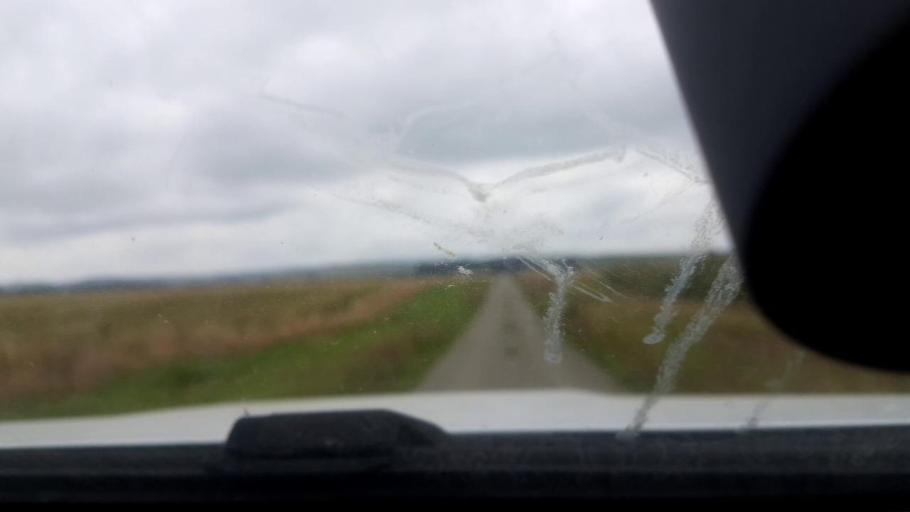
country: NZ
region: Canterbury
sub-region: Timaru District
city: Pleasant Point
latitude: -44.2324
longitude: 171.1670
